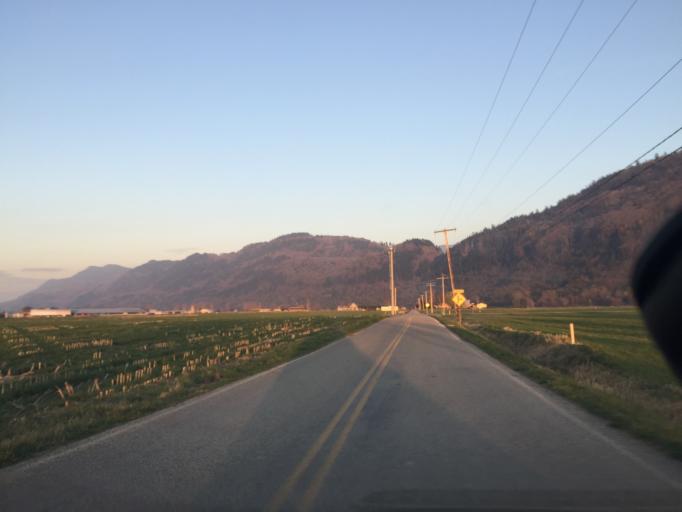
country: US
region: Washington
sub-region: Whatcom County
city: Peaceful Valley
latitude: 48.9999
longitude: -122.1860
